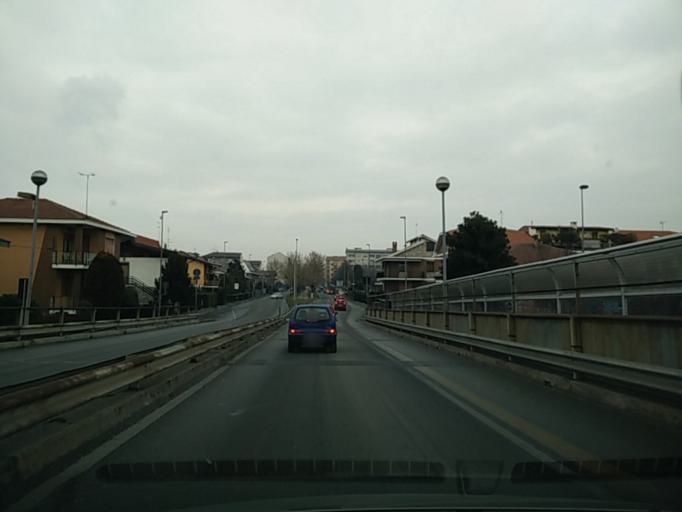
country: IT
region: Piedmont
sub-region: Provincia di Torino
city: Settimo Torinese
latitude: 45.1375
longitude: 7.7564
